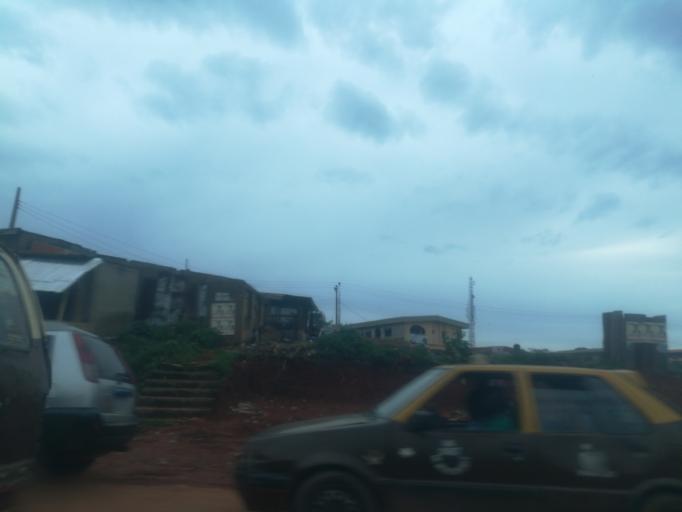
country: NG
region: Oyo
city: Ibadan
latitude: 7.3908
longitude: 3.9748
